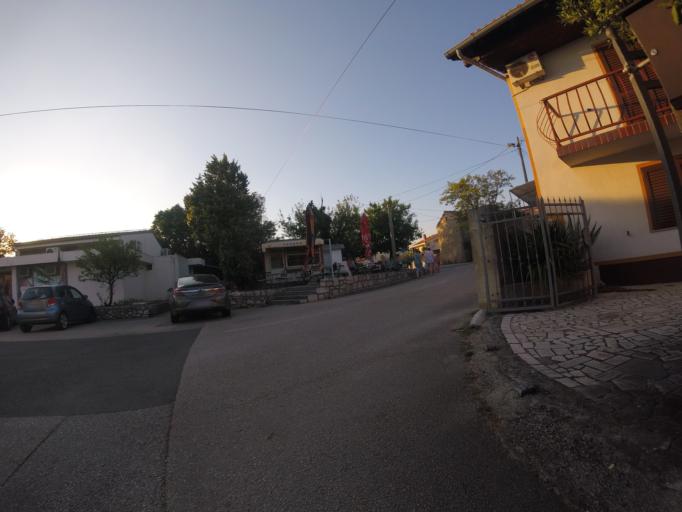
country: HR
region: Primorsko-Goranska
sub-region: Grad Crikvenica
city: Jadranovo
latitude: 45.2191
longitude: 14.6243
